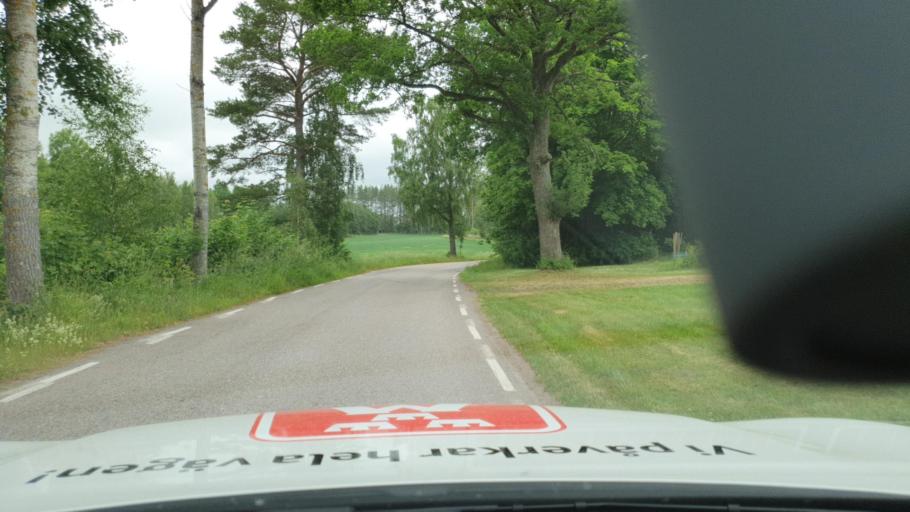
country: SE
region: Vaestra Goetaland
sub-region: Tibro Kommun
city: Tibro
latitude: 58.3503
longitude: 14.1564
